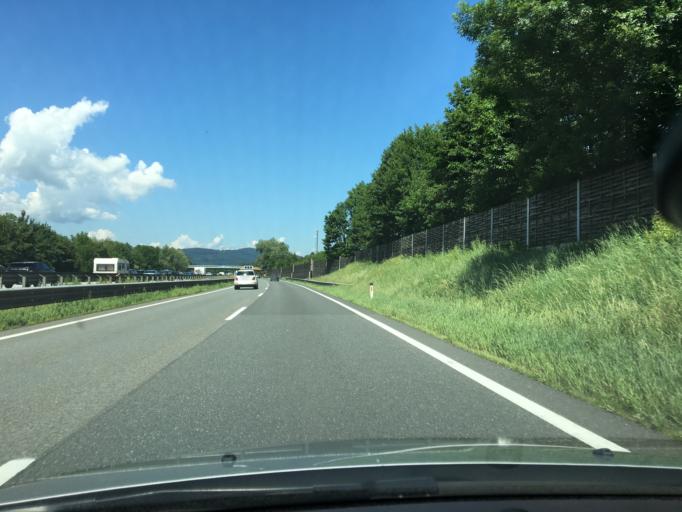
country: AT
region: Salzburg
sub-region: Politischer Bezirk Salzburg-Umgebung
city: Grodig
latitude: 47.7657
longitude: 12.9954
